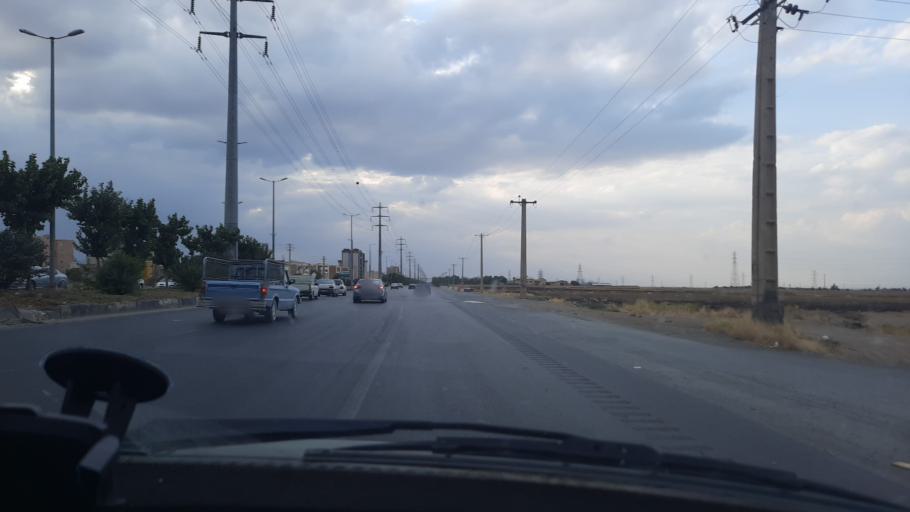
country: IR
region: Markazi
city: Arak
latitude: 34.1017
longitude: 49.7498
